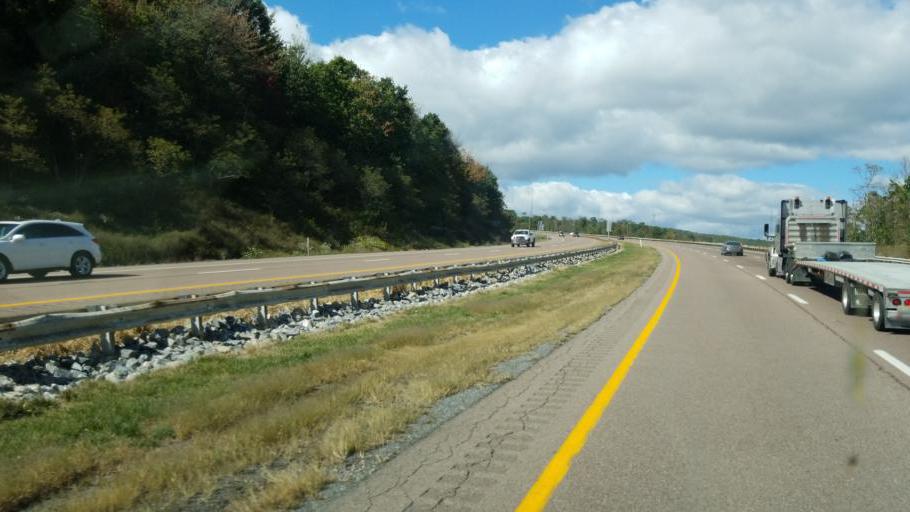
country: US
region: Maryland
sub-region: Allegany County
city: Frostburg
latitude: 39.6560
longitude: -78.9539
